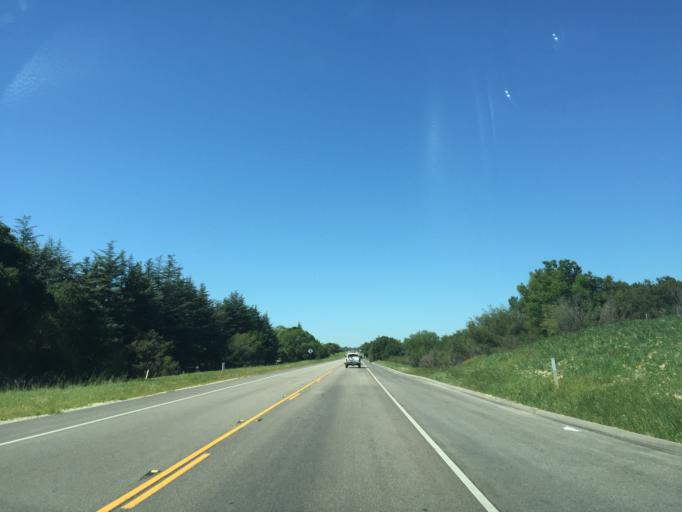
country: US
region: California
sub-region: Santa Barbara County
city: Santa Ynez
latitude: 34.6428
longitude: -120.0887
